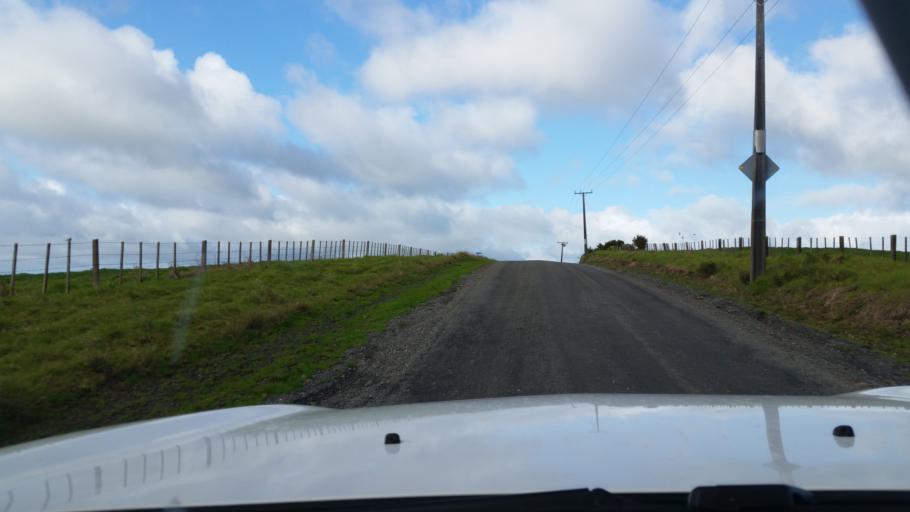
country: NZ
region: Northland
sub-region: Whangarei
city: Maungatapere
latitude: -35.6704
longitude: 174.1002
